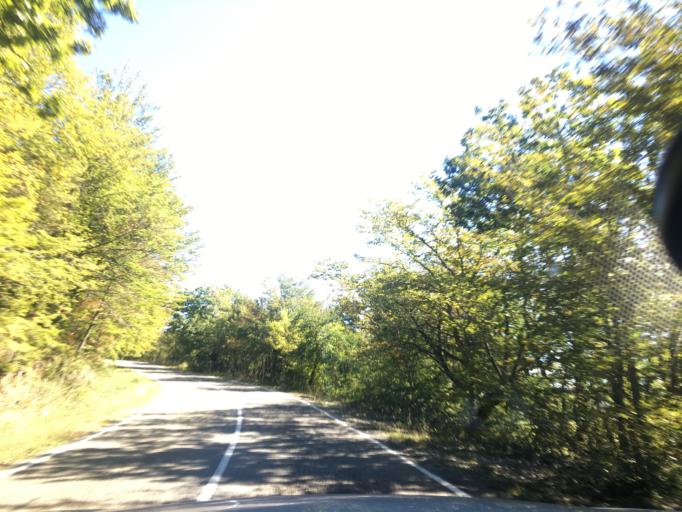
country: GE
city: Didi Lilo
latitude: 41.8846
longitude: 44.9189
